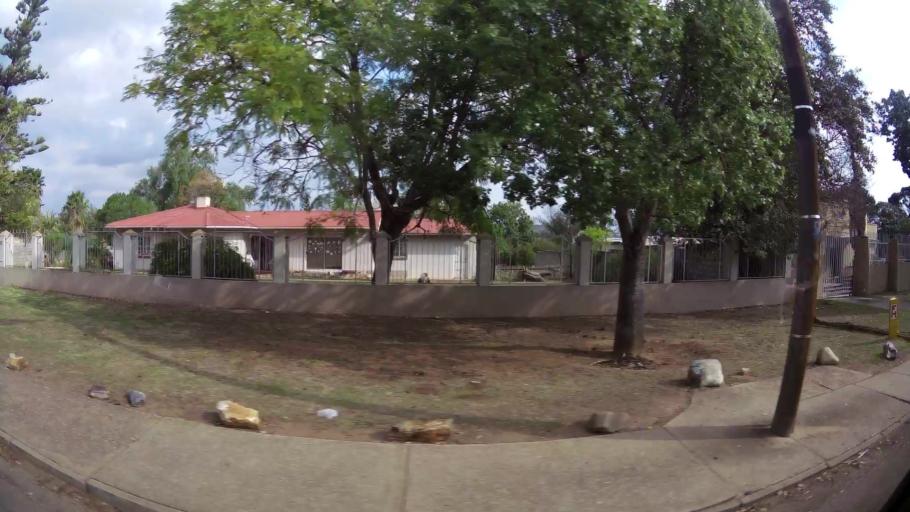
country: ZA
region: Eastern Cape
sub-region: Nelson Mandela Bay Metropolitan Municipality
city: Uitenhage
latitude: -33.7474
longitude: 25.4026
